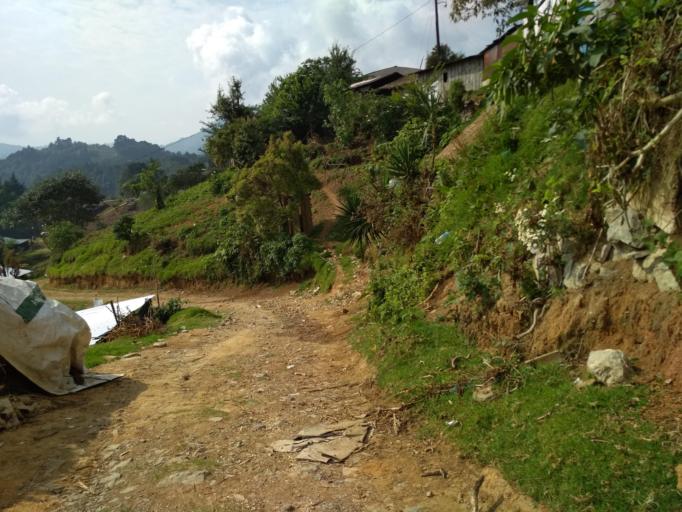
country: MX
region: Veracruz
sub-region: Soledad Atzompa
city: Tlatilpa
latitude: 18.7508
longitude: -97.1539
